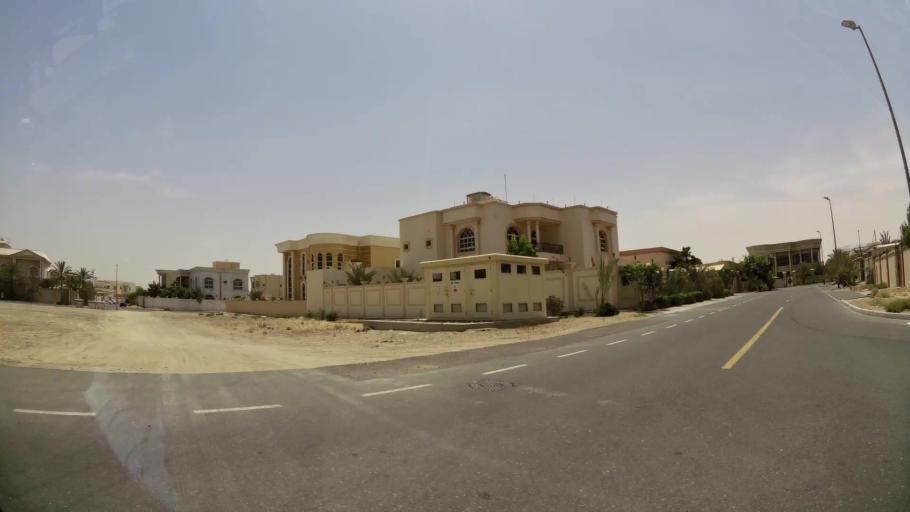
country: AE
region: Ash Shariqah
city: Sharjah
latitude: 25.1929
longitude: 55.4146
